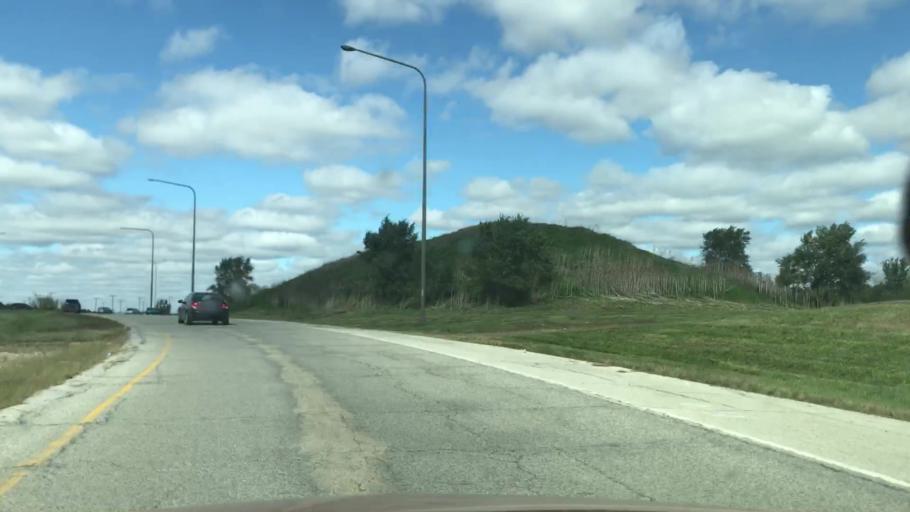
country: US
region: Illinois
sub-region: Cook County
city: Rosemont
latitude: 41.9839
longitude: -87.8774
